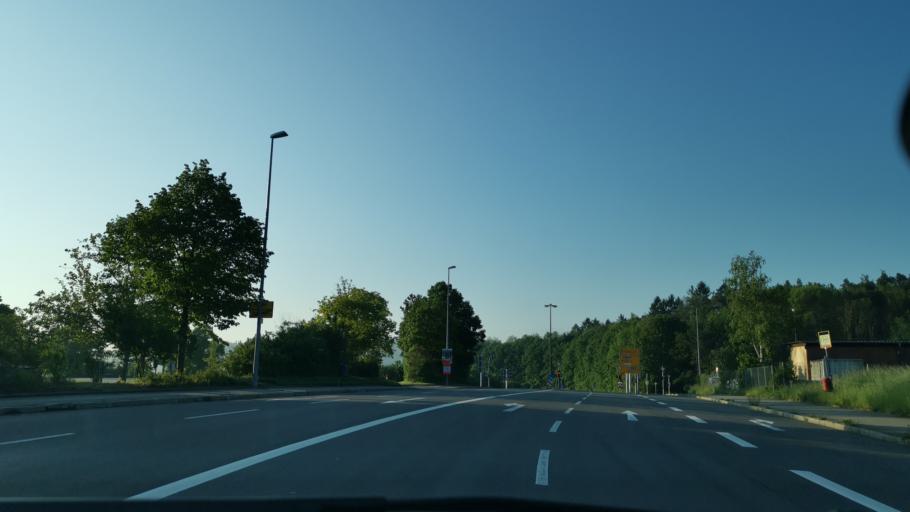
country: DE
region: Baden-Wuerttemberg
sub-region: Regierungsbezirk Stuttgart
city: Boeblingen
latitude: 48.6756
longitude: 8.9759
